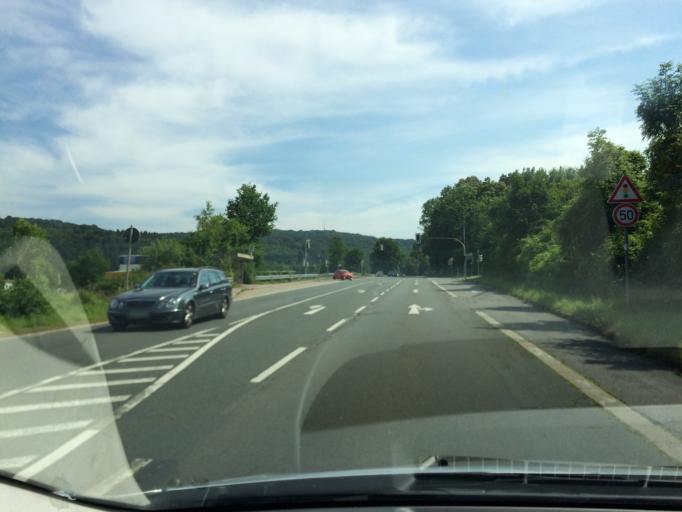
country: DE
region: North Rhine-Westphalia
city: Iserlohn
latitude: 51.3852
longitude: 7.7247
